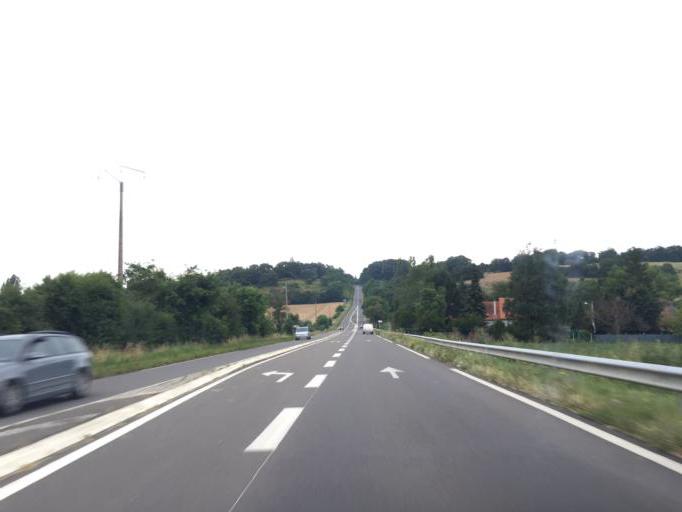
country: FR
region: Auvergne
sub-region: Departement de l'Allier
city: Brugheas
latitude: 46.1127
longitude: 3.3297
